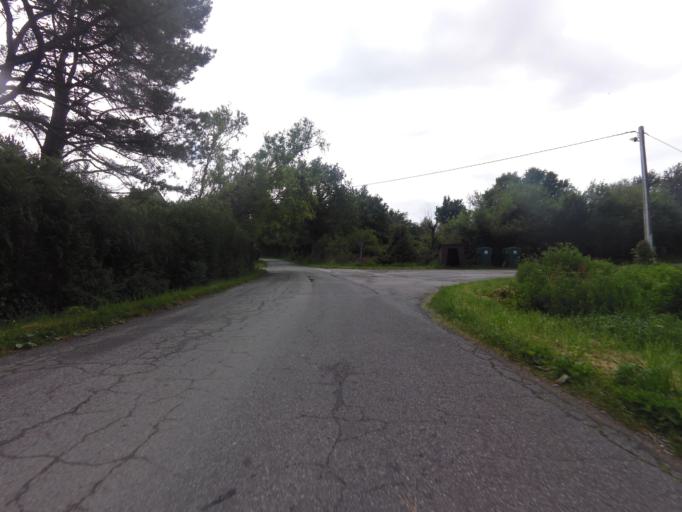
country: FR
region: Brittany
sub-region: Departement du Morbihan
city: Baden
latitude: 47.6029
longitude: -2.9380
